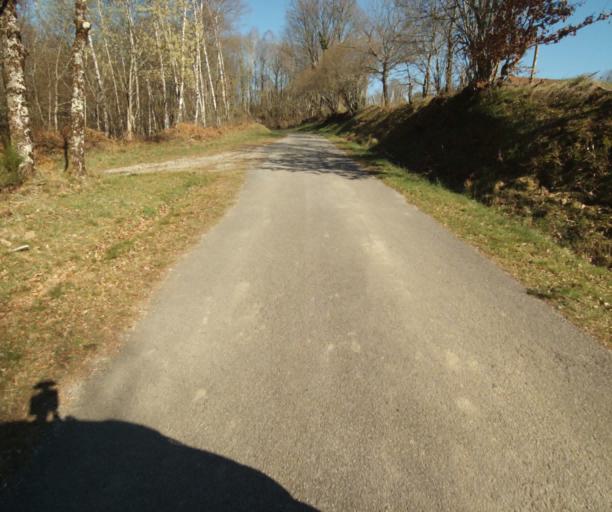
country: FR
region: Limousin
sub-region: Departement de la Correze
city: Chamboulive
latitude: 45.4848
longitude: 1.6982
